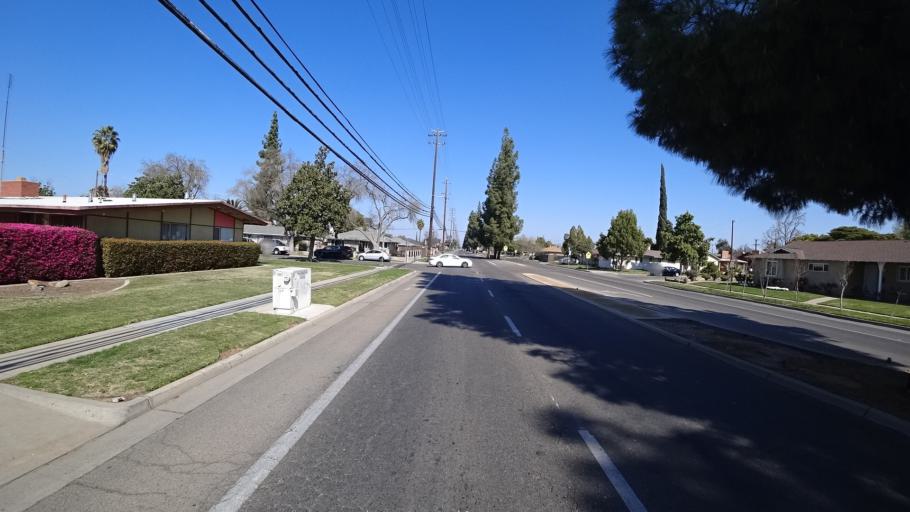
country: US
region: California
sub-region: Fresno County
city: Fresno
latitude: 36.7671
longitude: -119.8268
